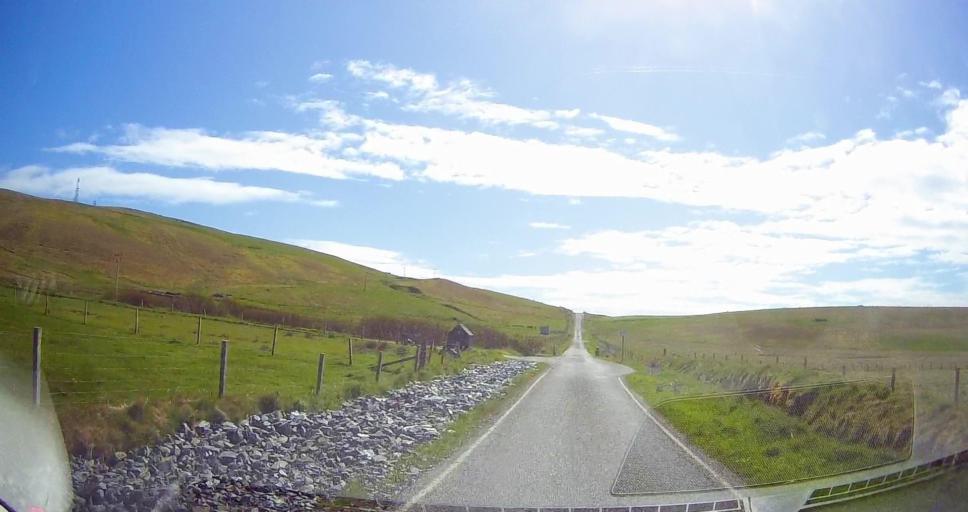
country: GB
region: Scotland
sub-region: Shetland Islands
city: Sandwick
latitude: 59.9647
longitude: -1.3212
